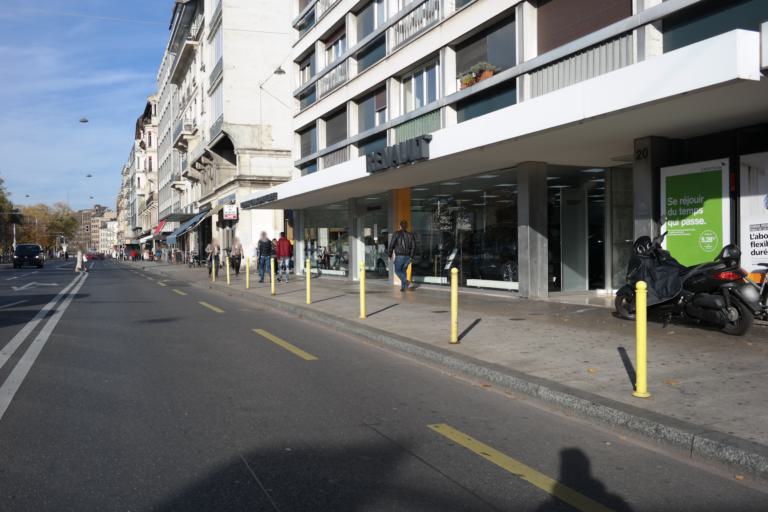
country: CH
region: Geneva
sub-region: Geneva
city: Geneve
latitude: 46.1969
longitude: 6.1419
